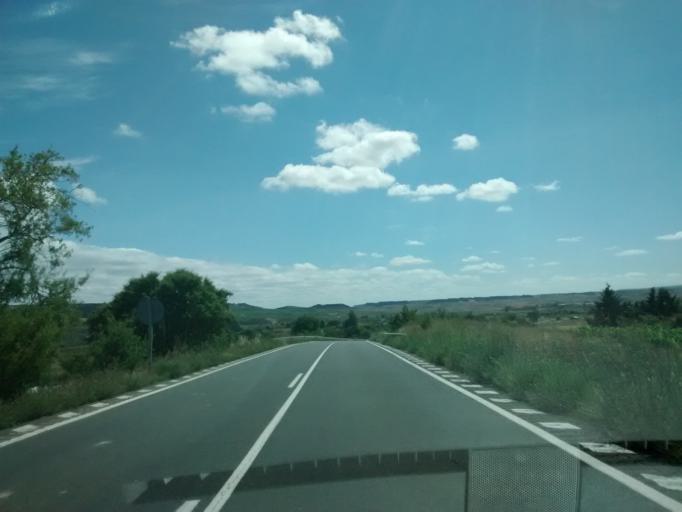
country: ES
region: La Rioja
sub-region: Provincia de La Rioja
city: Villamediana de Iregua
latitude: 42.4216
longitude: -2.4039
